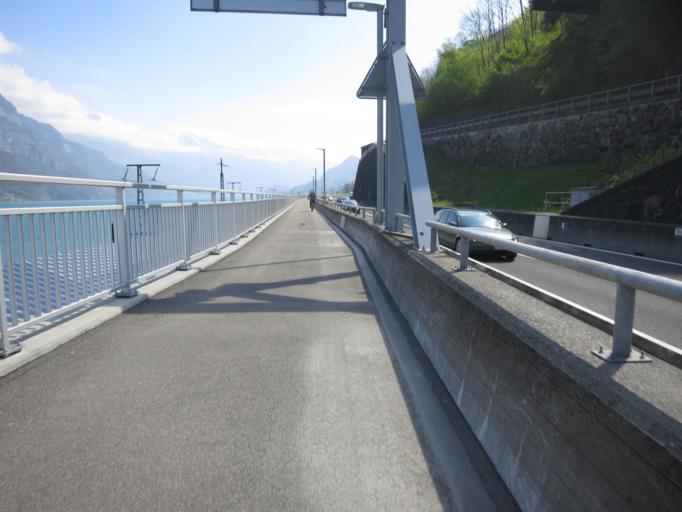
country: CH
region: Saint Gallen
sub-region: Wahlkreis See-Gaster
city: Amden
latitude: 47.1169
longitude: 9.1765
